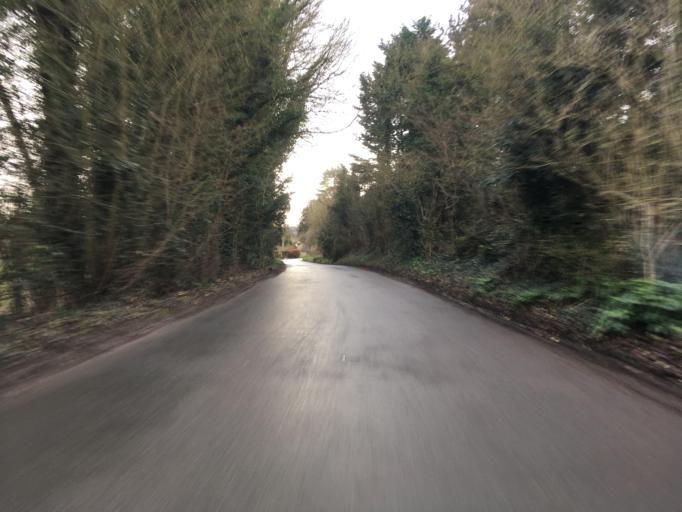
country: GB
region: England
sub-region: Gloucestershire
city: Gotherington
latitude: 52.0225
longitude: -2.0336
